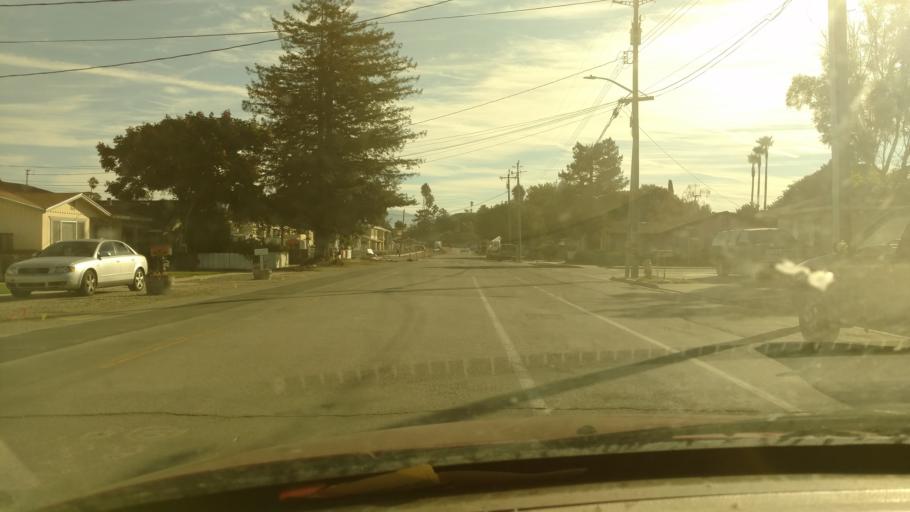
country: US
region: California
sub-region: San Benito County
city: Hollister
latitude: 36.8572
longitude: -121.4141
